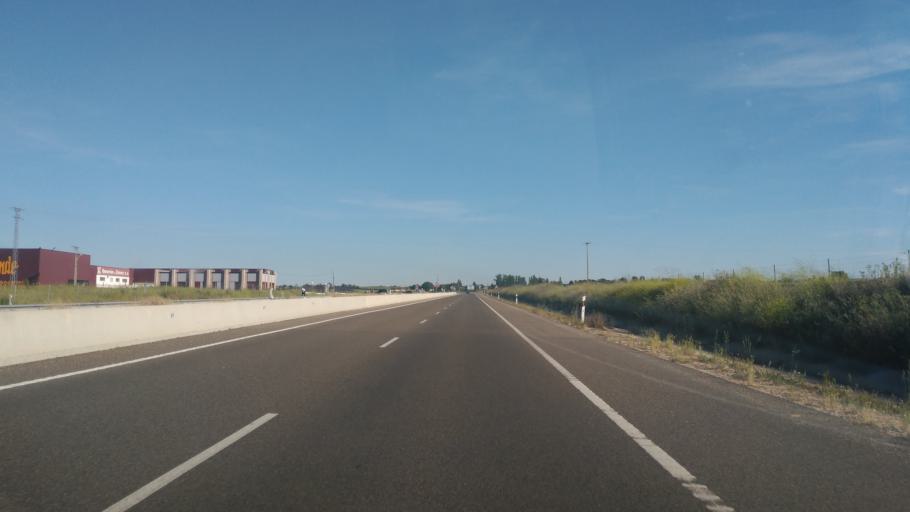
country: ES
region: Castille and Leon
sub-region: Provincia de Zamora
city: Morales del Vino
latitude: 41.4635
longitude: -5.7340
